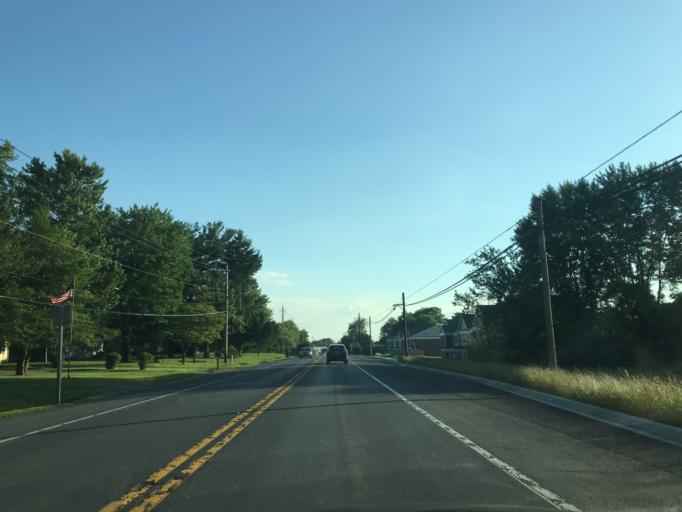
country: US
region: Maryland
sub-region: Talbot County
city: Easton
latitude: 38.7810
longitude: -76.0537
